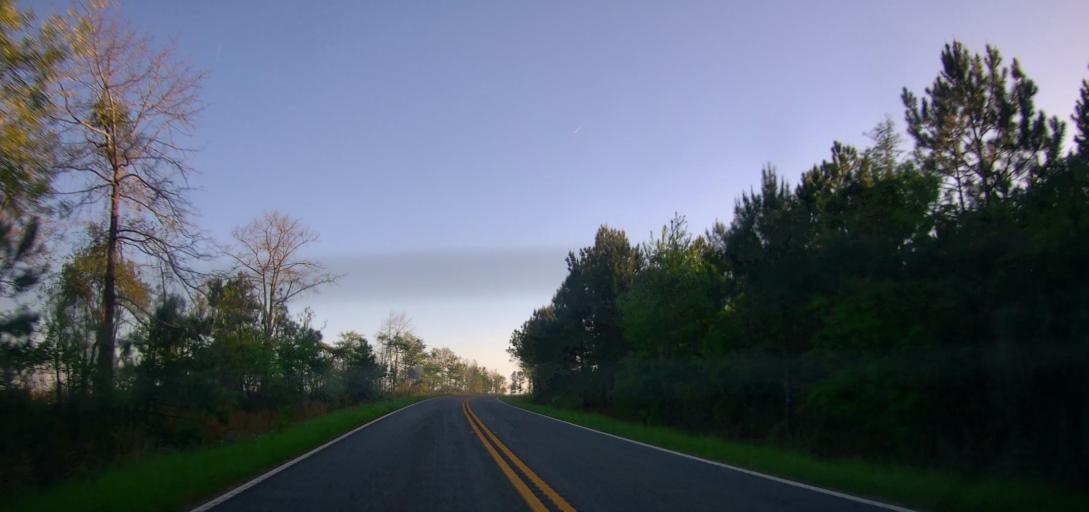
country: US
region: Georgia
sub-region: Marion County
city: Buena Vista
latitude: 32.4311
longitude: -84.4282
